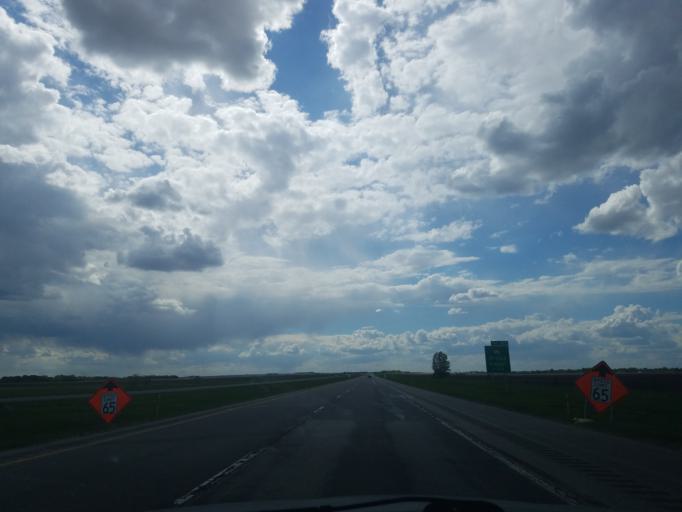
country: US
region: North Dakota
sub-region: Barnes County
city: Valley City
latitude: 46.9203
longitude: -97.7617
